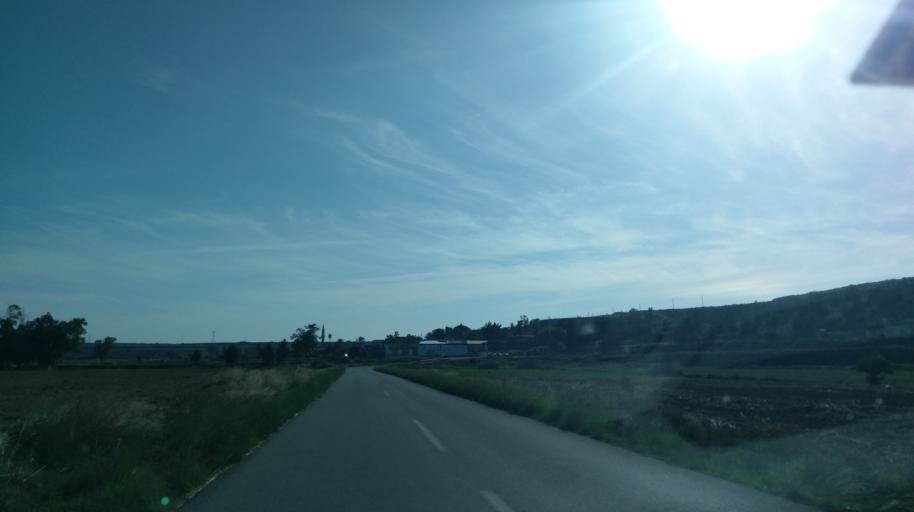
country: CY
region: Ammochostos
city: Trikomo
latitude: 35.2785
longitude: 33.8527
